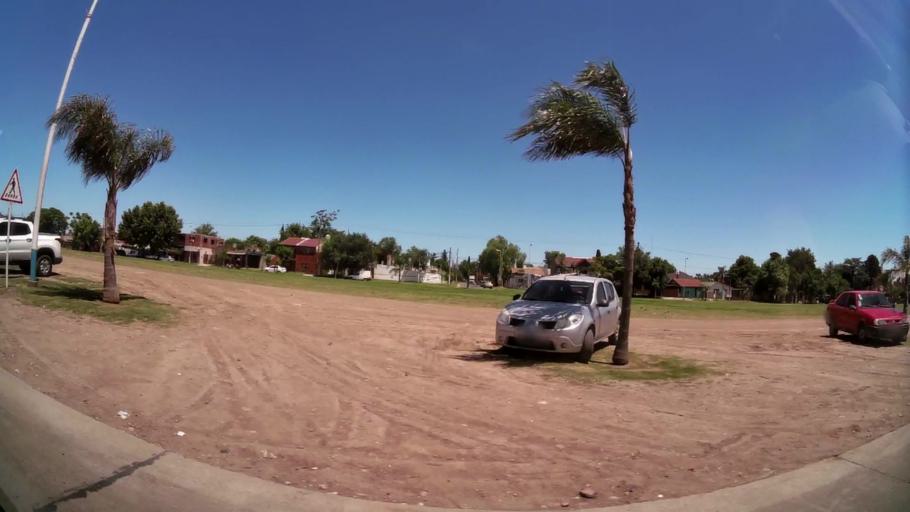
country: AR
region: Buenos Aires
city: Hurlingham
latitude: -34.4978
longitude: -58.7026
